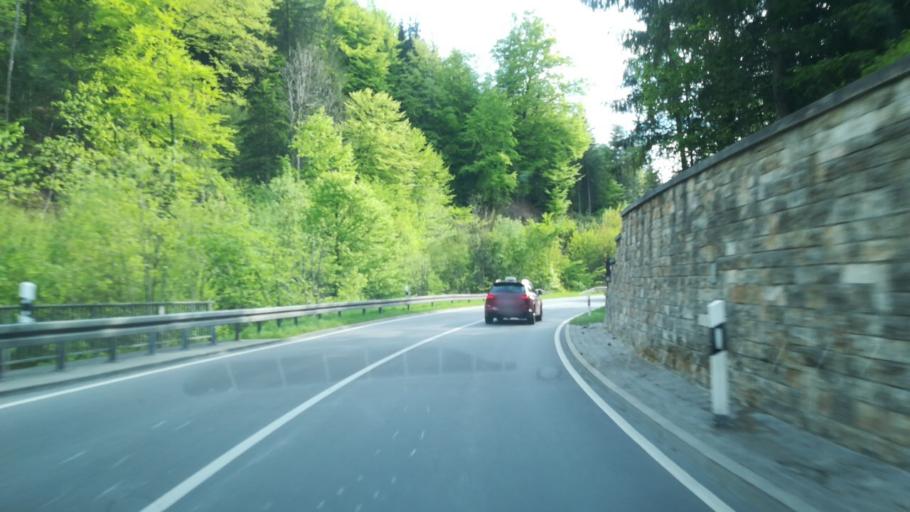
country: DE
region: Baden-Wuerttemberg
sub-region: Freiburg Region
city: Muhlingen
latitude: 47.9016
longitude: 9.0133
